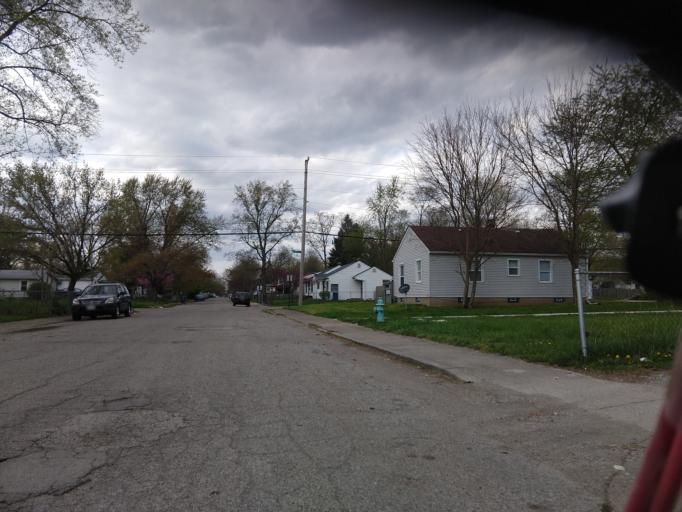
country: US
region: Indiana
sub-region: Marion County
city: Broad Ripple
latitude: 39.8361
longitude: -86.1301
